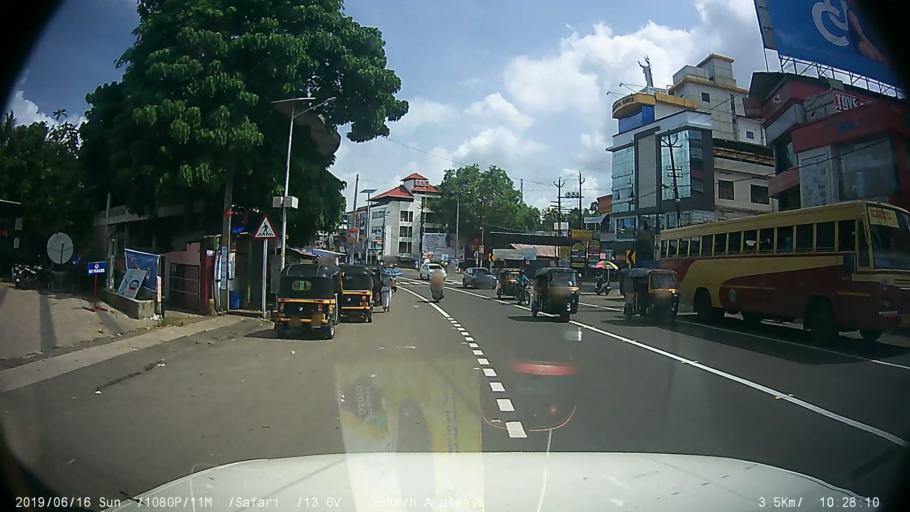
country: IN
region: Kerala
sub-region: Kottayam
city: Changanacheri
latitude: 9.4425
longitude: 76.5441
